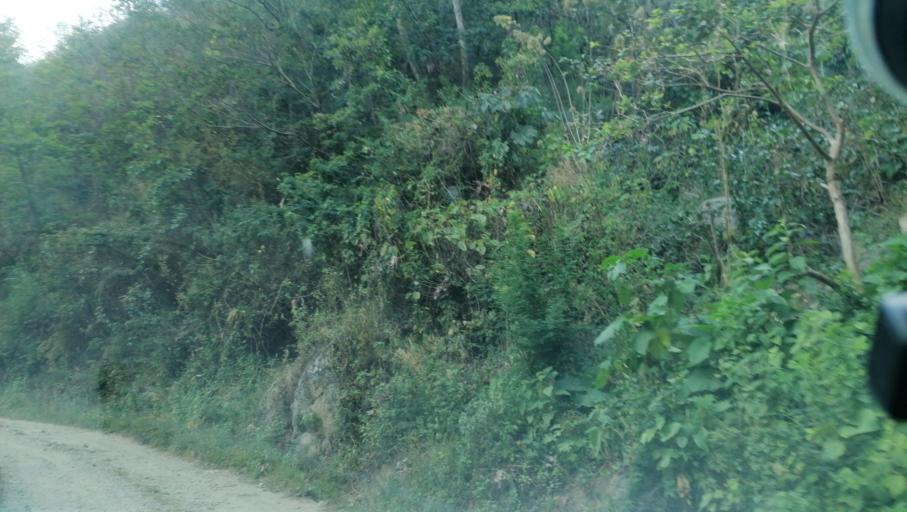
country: MX
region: Chiapas
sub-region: Cacahoatan
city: Benito Juarez
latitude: 15.1471
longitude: -92.1863
